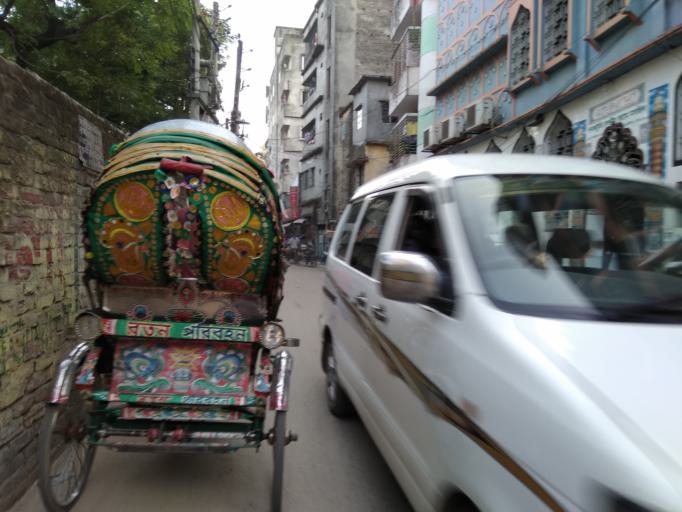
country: BD
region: Dhaka
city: Azimpur
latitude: 23.7278
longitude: 90.3766
